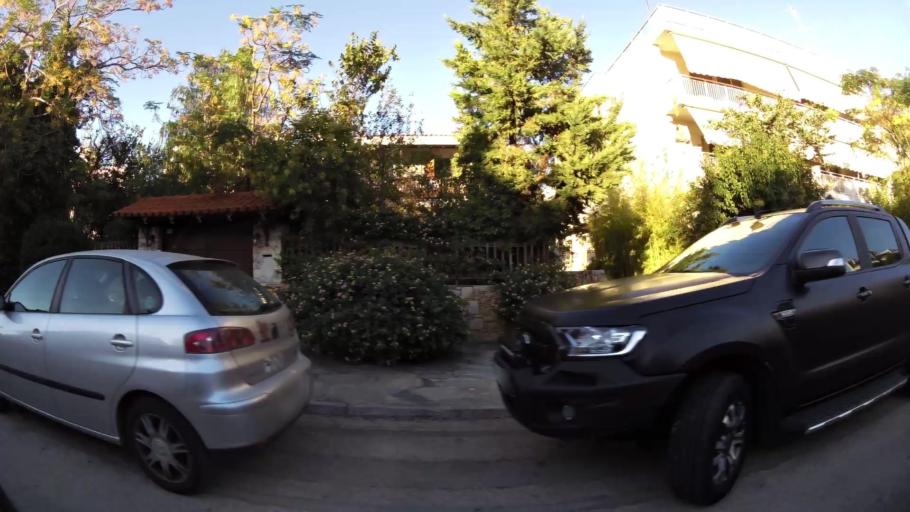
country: GR
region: Attica
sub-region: Nomarchia Athinas
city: Glyfada
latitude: 37.8672
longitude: 23.7515
